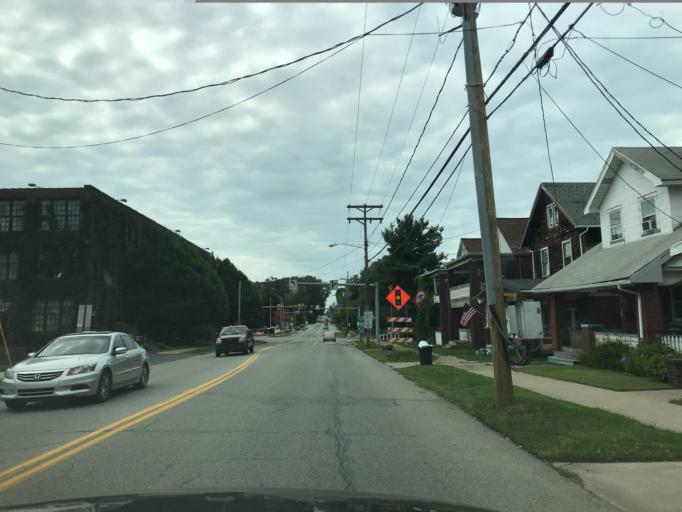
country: US
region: Pennsylvania
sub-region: Erie County
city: Erie
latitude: 42.1162
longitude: -80.1145
